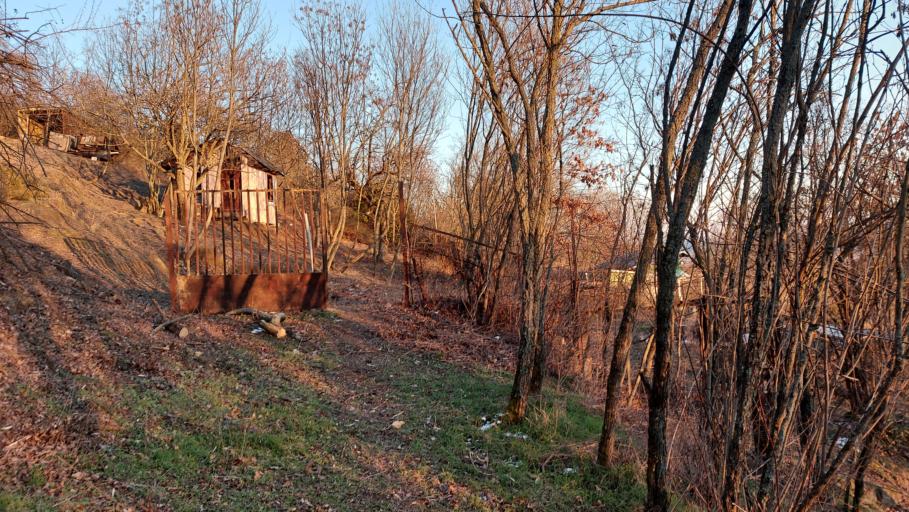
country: HU
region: Pest
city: Budaors
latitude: 47.4736
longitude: 18.9536
